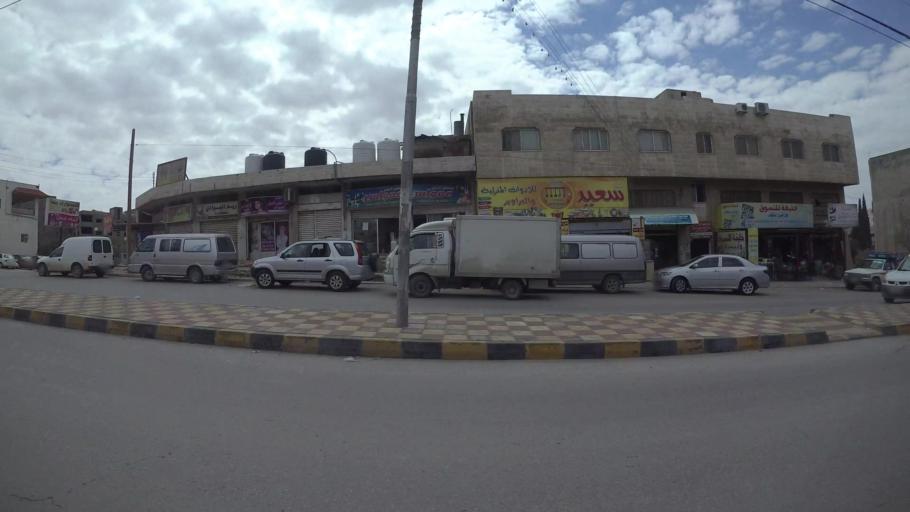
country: JO
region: Amman
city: Al Jubayhah
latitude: 32.0576
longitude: 35.8336
